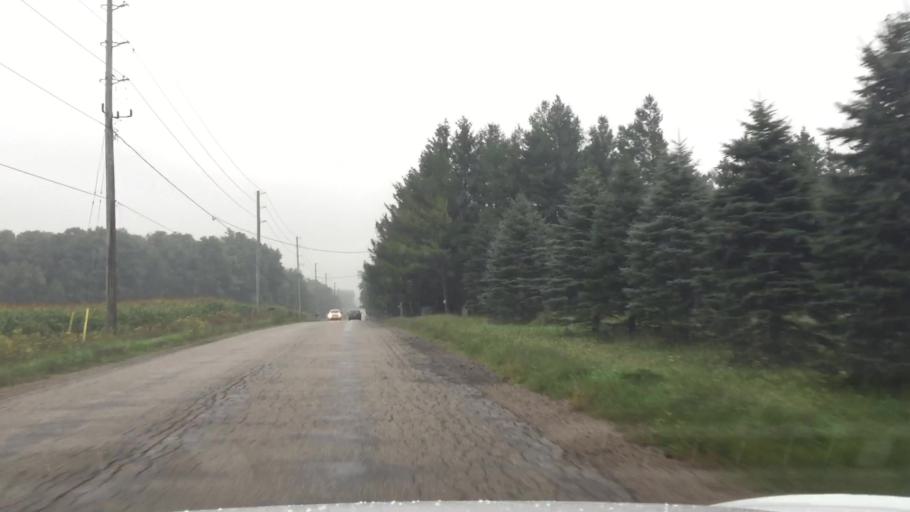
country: CA
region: Ontario
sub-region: Oxford County
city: Woodstock
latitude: 43.1118
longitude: -80.7104
